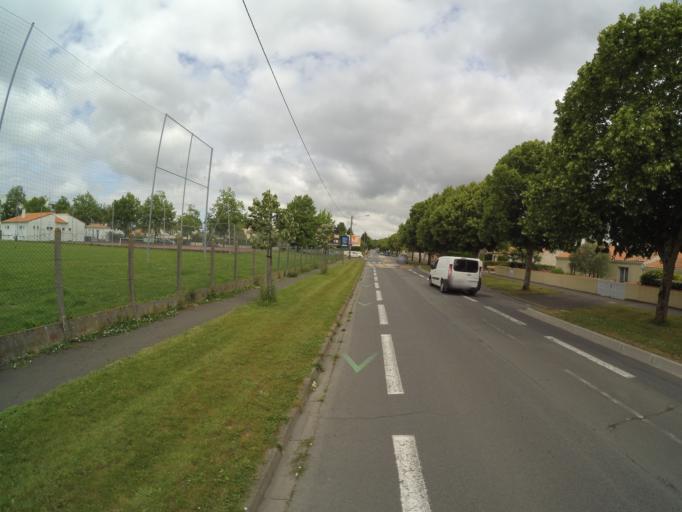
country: FR
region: Poitou-Charentes
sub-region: Departement de la Charente-Maritime
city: Rochefort
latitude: 45.9549
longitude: -0.9691
